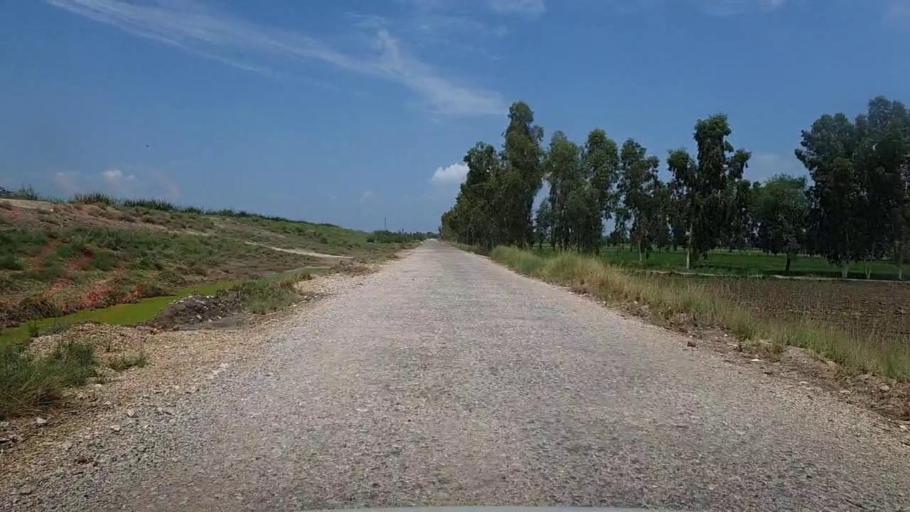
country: PK
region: Sindh
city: Bhiria
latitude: 26.9168
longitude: 68.2060
